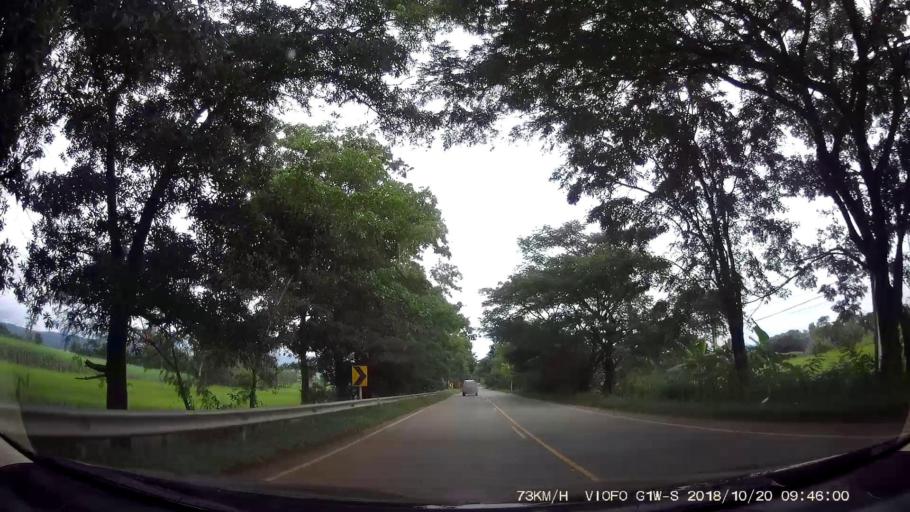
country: TH
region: Chaiyaphum
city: Khon San
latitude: 16.4929
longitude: 101.9301
